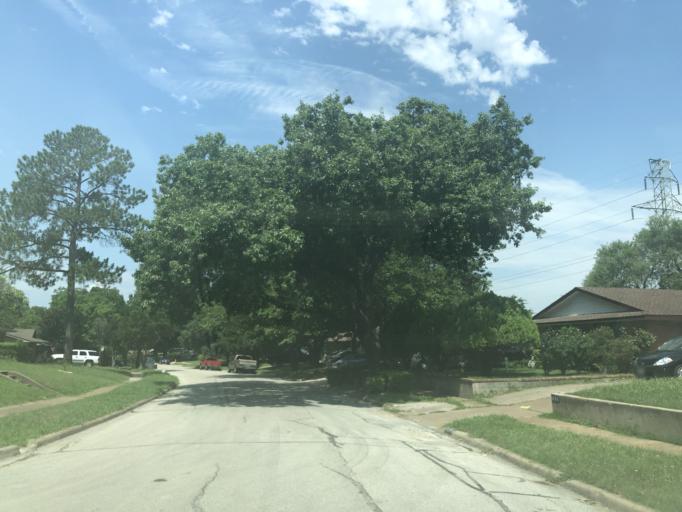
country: US
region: Texas
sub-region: Dallas County
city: Grand Prairie
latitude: 32.7242
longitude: -97.0110
